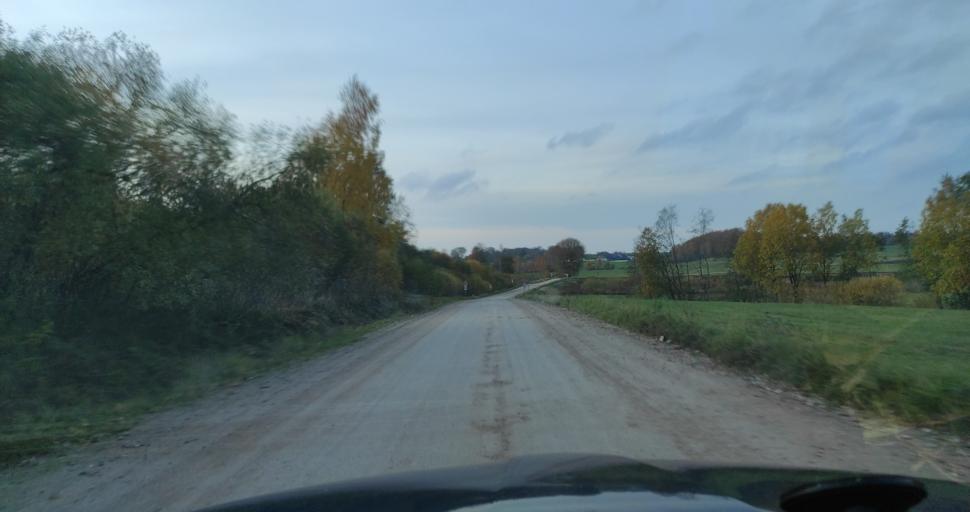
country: LV
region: Aizpute
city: Aizpute
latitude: 56.6463
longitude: 21.7986
